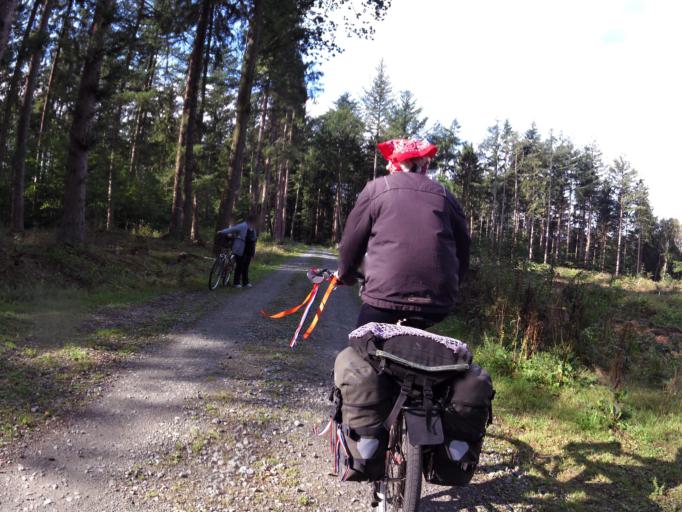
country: DE
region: Lower Saxony
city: Bremervorde
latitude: 53.4726
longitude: 9.1469
